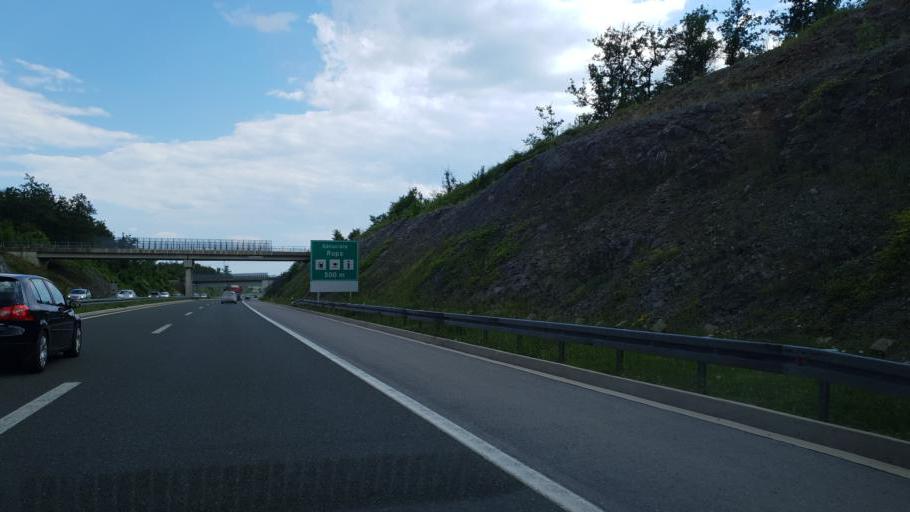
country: HR
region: Primorsko-Goranska
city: Matulji
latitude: 45.4516
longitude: 14.2709
